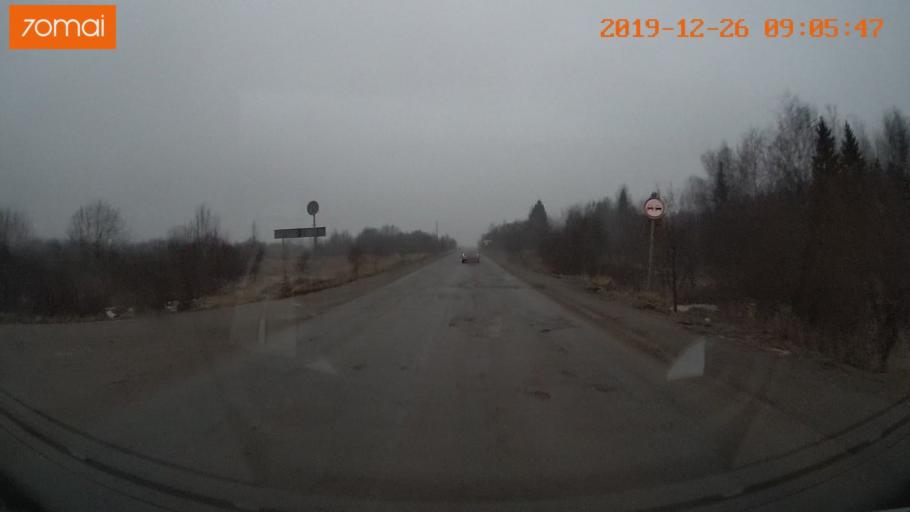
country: RU
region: Vologda
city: Gryazovets
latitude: 58.8292
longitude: 40.2563
